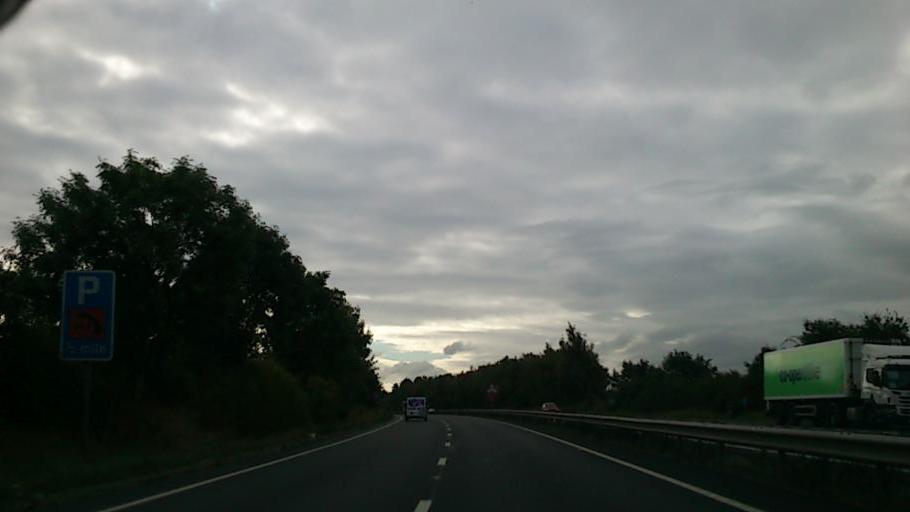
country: GB
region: England
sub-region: Shropshire
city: Great Hanwood
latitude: 52.6957
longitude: -2.8069
